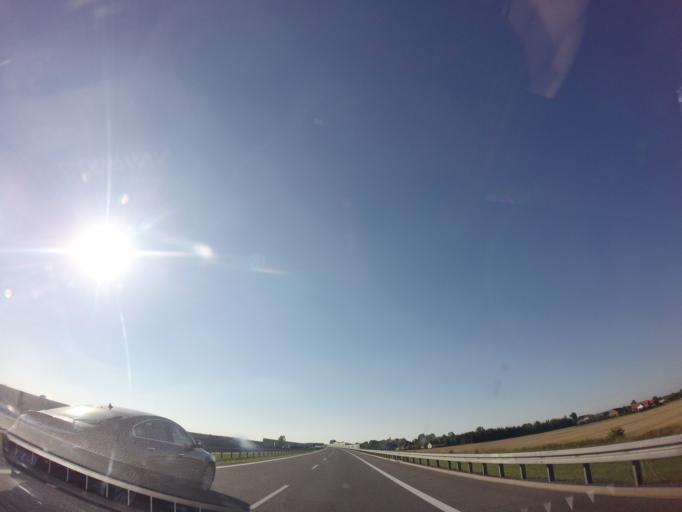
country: PL
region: Lubusz
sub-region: Powiat gorzowski
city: Deszczno
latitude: 52.6845
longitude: 15.2879
